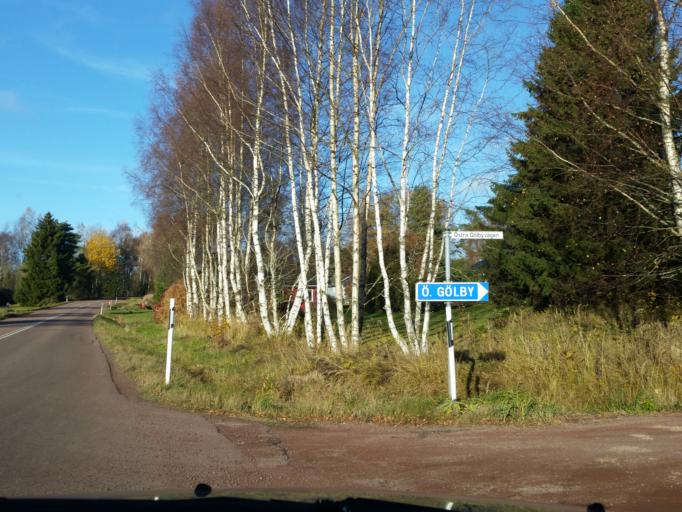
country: AX
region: Alands landsbygd
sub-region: Jomala
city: Jomala
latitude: 60.1919
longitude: 19.9473
